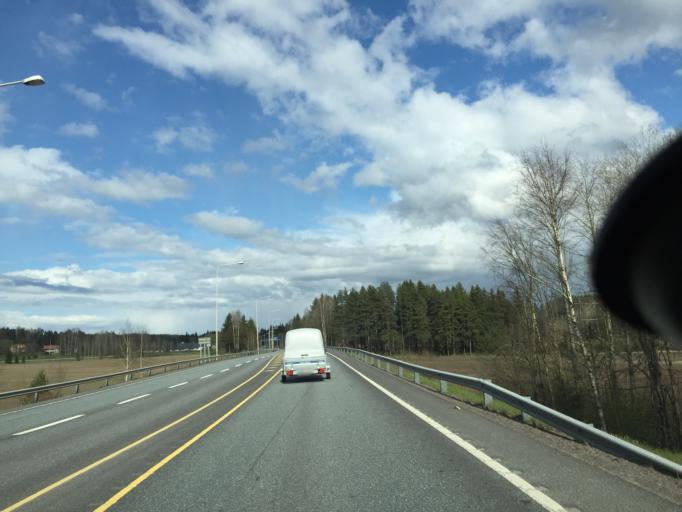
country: FI
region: Uusimaa
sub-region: Raaseporin
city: Karis
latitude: 60.0681
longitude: 23.6943
